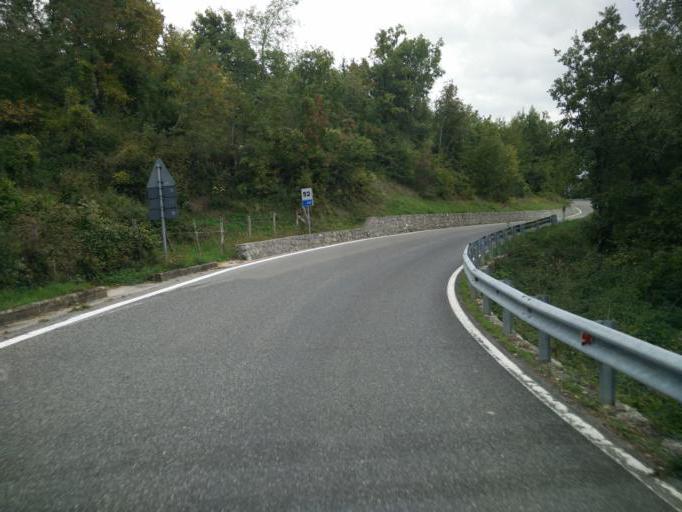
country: IT
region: Tuscany
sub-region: Provincia di Lucca
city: Giuncugnano
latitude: 44.2073
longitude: 10.2222
